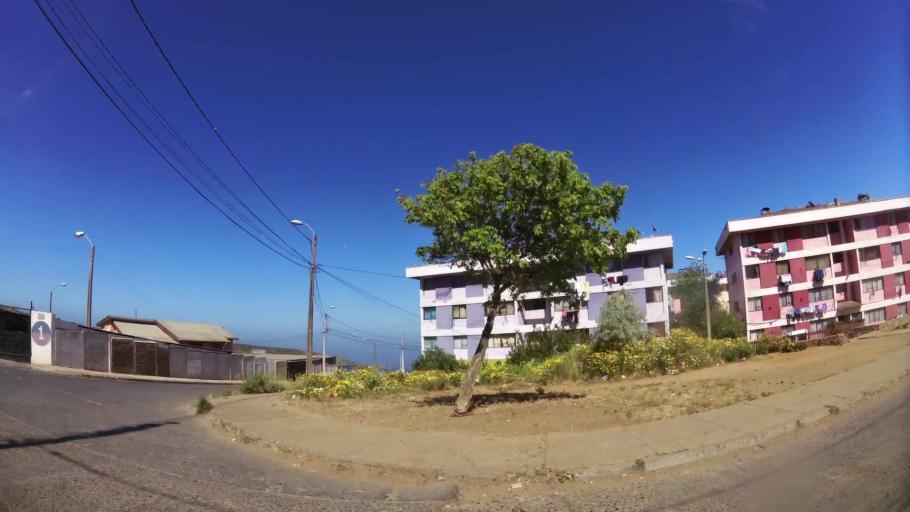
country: CL
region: Valparaiso
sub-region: Provincia de Valparaiso
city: Valparaiso
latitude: -33.0553
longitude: -71.6509
